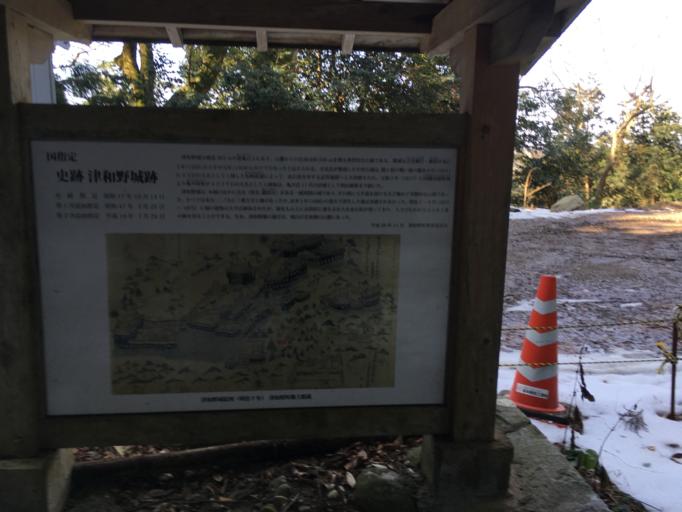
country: JP
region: Shimane
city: Masuda
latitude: 34.4611
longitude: 131.7641
